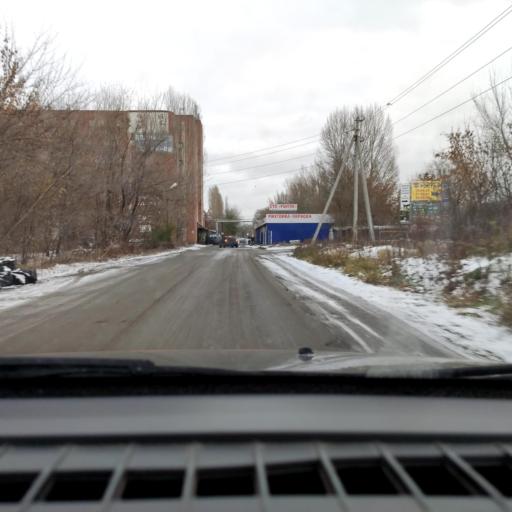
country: RU
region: Samara
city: Tol'yatti
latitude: 53.5450
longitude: 49.2897
